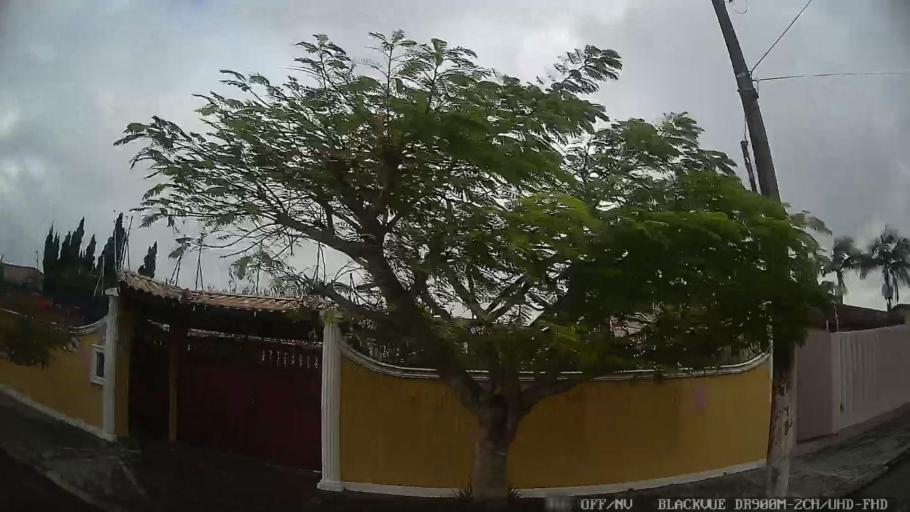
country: BR
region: Sao Paulo
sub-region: Itanhaem
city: Itanhaem
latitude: -24.2161
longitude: -46.8471
